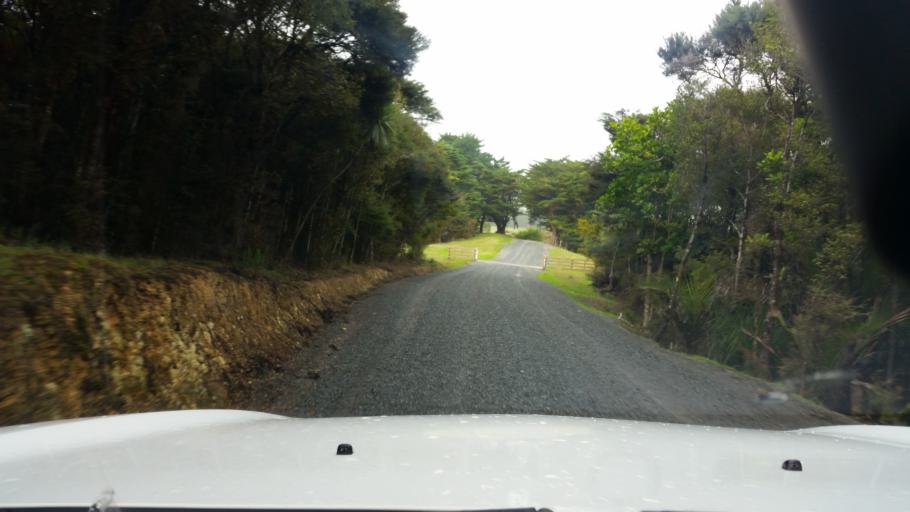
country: NZ
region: Northland
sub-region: Whangarei
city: Ruakaka
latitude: -35.7764
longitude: 174.5423
